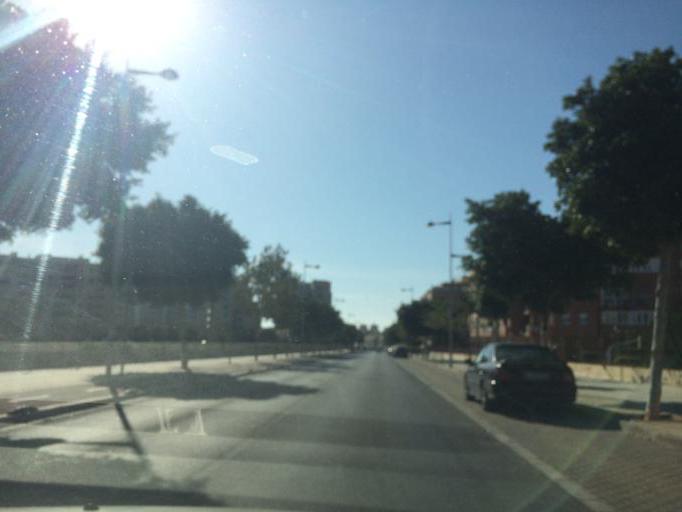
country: ES
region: Andalusia
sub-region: Provincia de Almeria
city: Almeria
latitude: 36.8348
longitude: -2.4422
